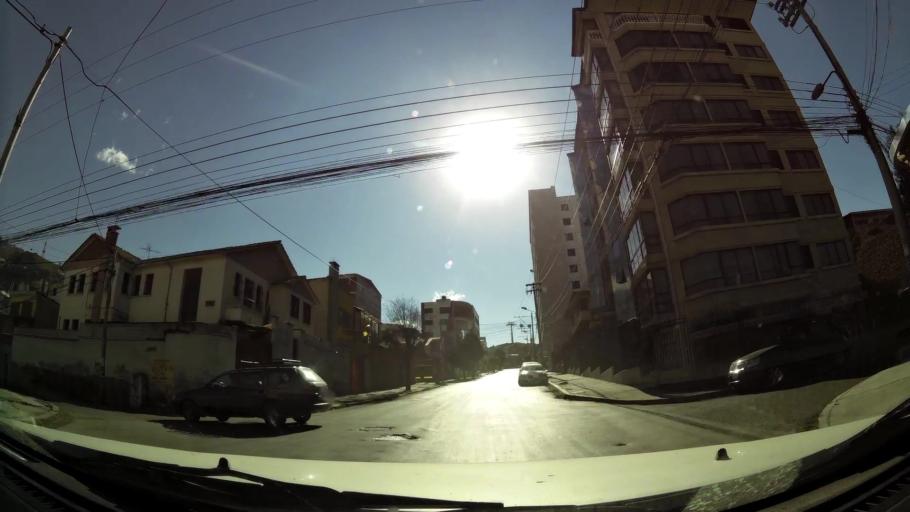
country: BO
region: La Paz
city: La Paz
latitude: -16.5166
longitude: -68.1316
